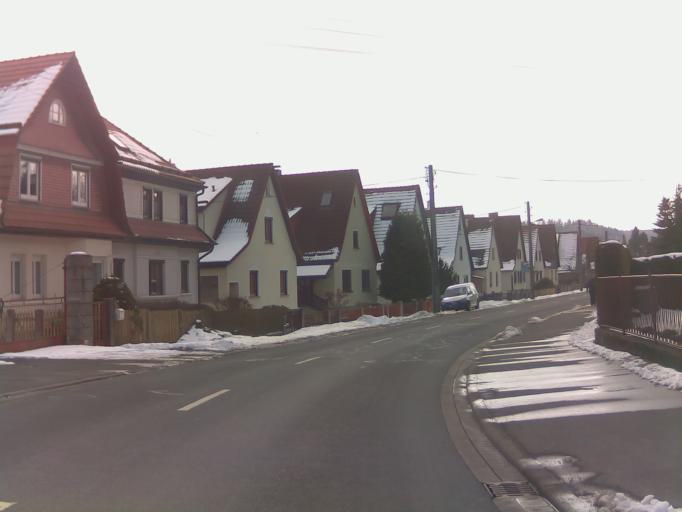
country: DE
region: Thuringia
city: Benshausen
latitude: 50.6400
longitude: 10.5900
